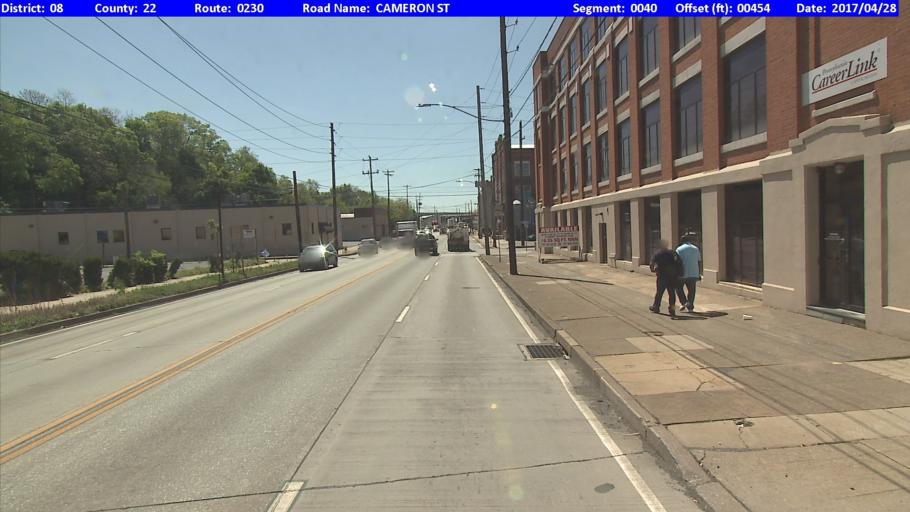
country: US
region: Pennsylvania
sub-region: Dauphin County
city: Harrisburg
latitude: 40.2667
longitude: -76.8754
